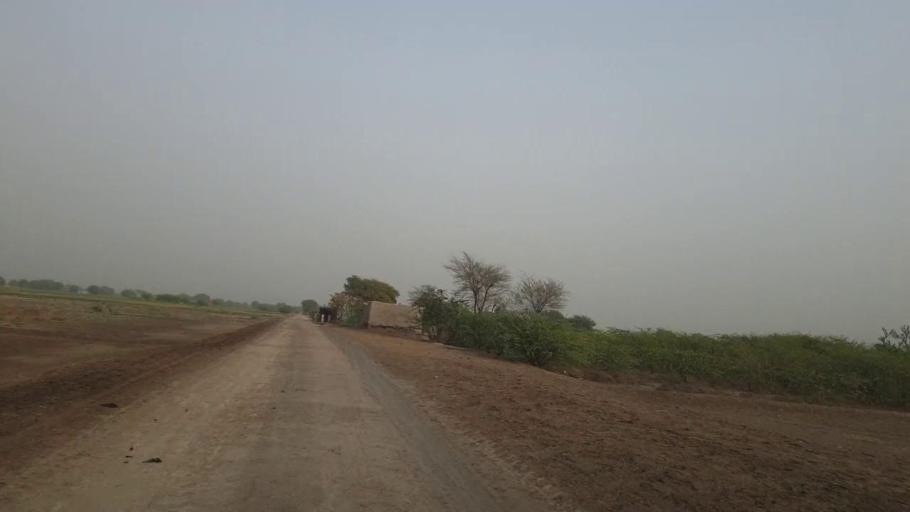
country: PK
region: Sindh
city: Kunri
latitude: 25.0968
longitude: 69.4405
